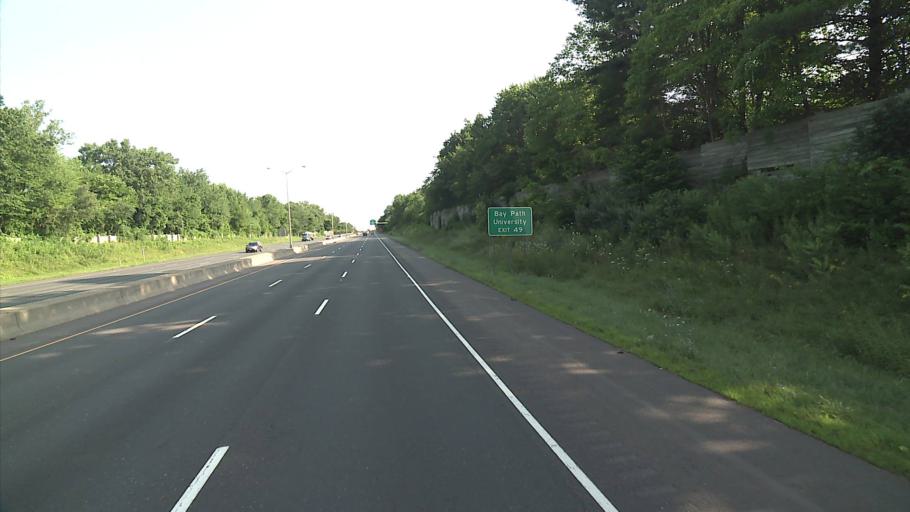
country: US
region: Connecticut
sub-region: Hartford County
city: Thompsonville
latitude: 42.0078
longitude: -72.5855
